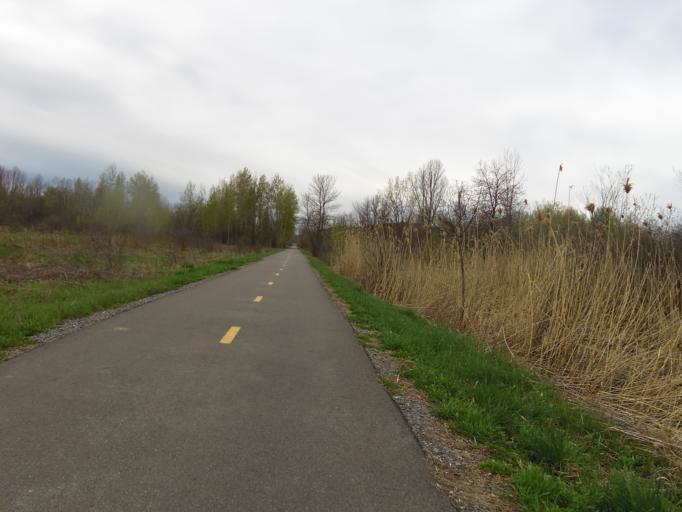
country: CA
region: Quebec
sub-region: Laurentides
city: Sainte-Marthe-sur-le-Lac
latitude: 45.4967
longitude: -73.9909
